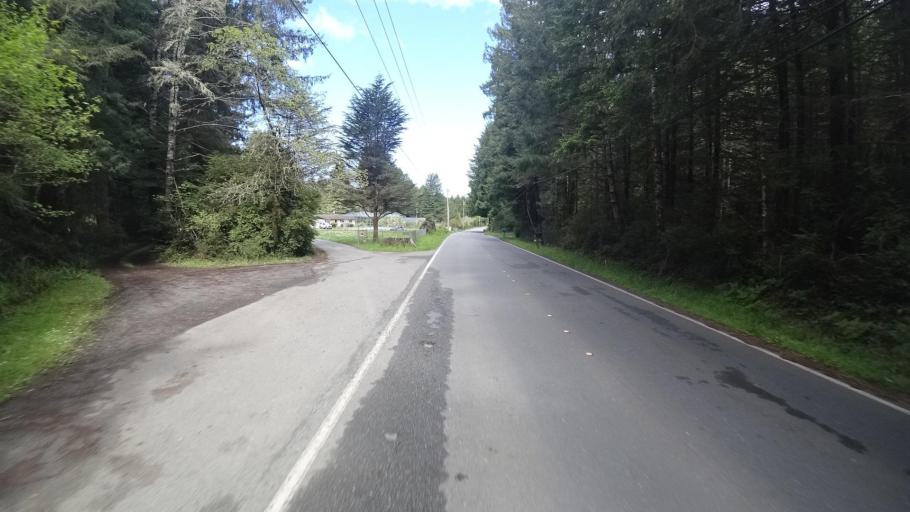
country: US
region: California
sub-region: Humboldt County
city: Blue Lake
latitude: 40.9425
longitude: -124.0260
